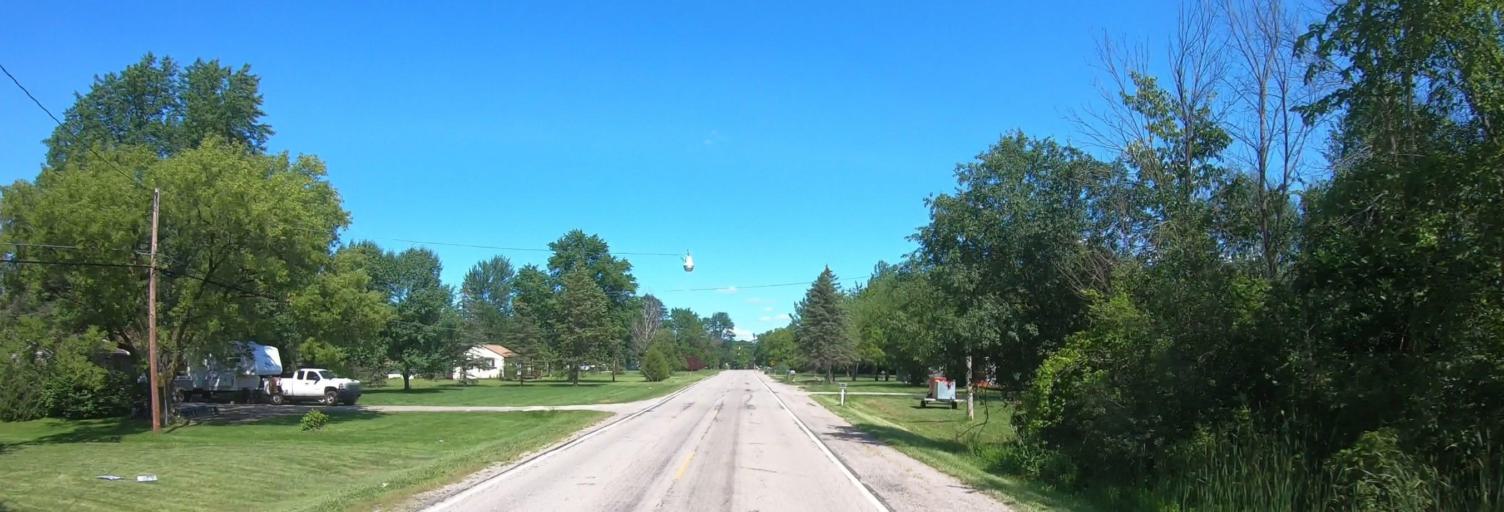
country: US
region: Michigan
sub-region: Genesee County
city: Flushing
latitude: 43.0786
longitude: -83.7776
